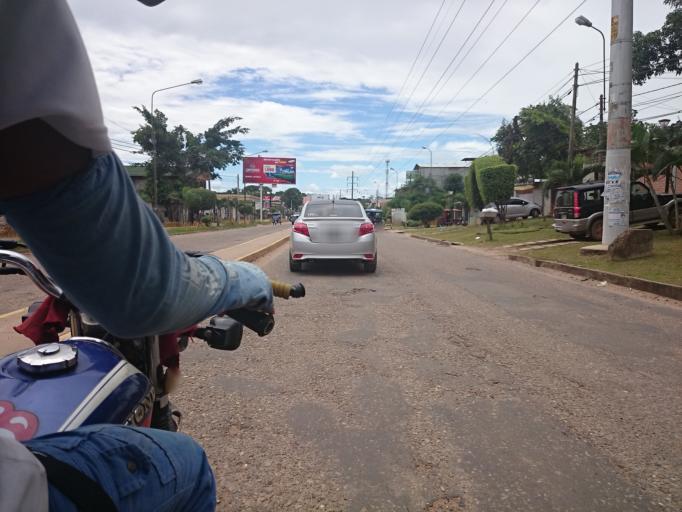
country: PE
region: Ucayali
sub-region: Provincia de Coronel Portillo
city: Pucallpa
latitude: -8.3695
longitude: -74.5606
